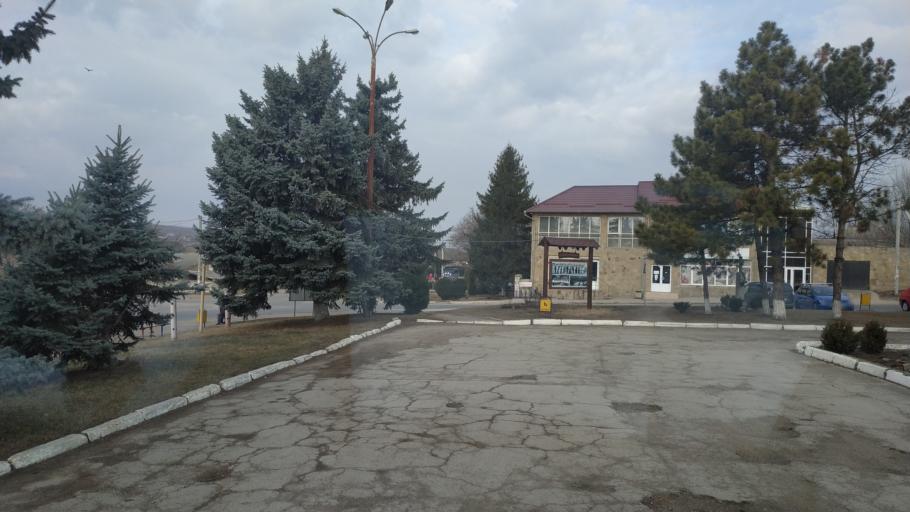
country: MD
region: Chisinau
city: Singera
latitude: 46.9633
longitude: 29.0564
